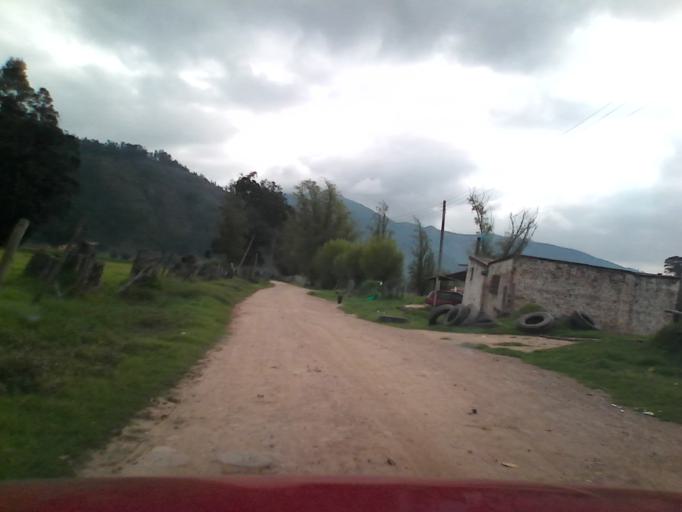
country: CO
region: Boyaca
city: Duitama
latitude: 5.8102
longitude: -73.0061
